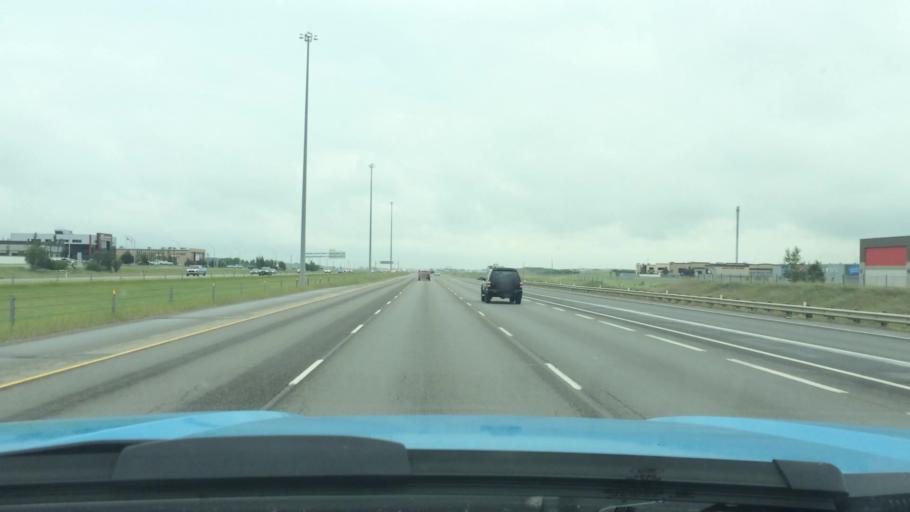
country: CA
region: Alberta
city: Airdrie
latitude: 51.2631
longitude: -114.0017
